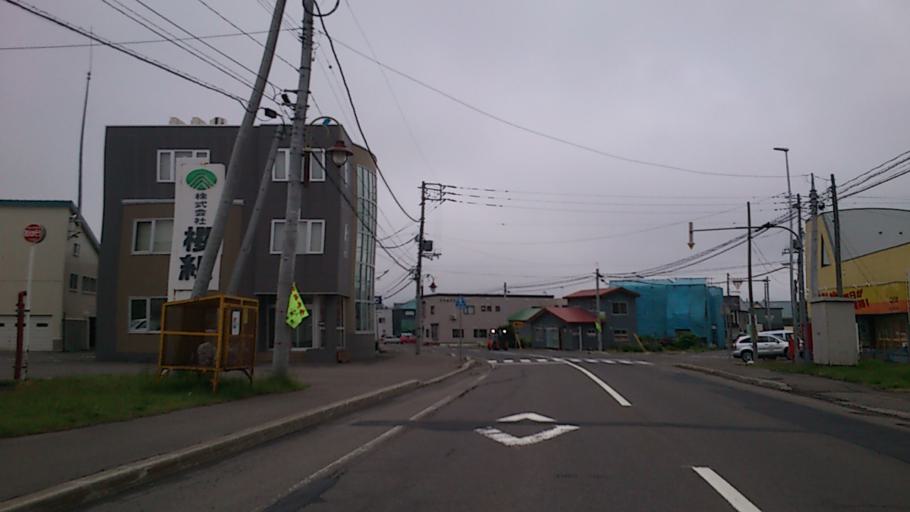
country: JP
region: Hokkaido
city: Niseko Town
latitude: 42.8567
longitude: 140.8898
